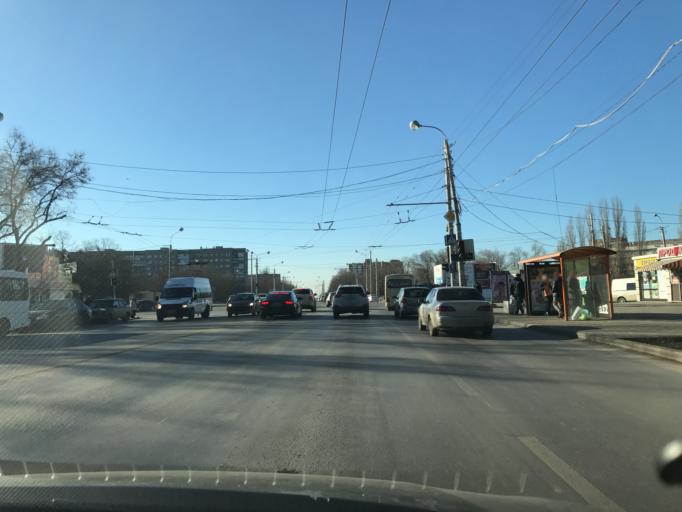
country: RU
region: Rostov
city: Rostov-na-Donu
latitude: 47.2125
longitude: 39.6358
